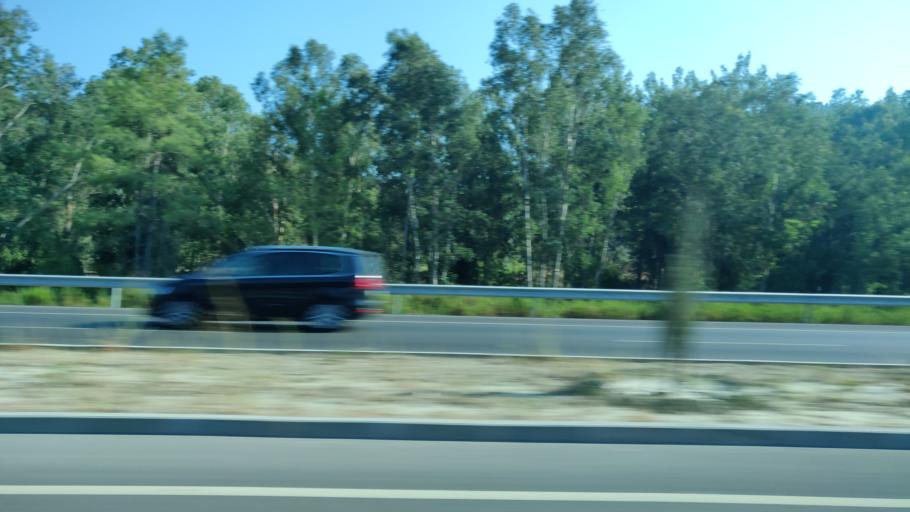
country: TR
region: Mugla
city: Goecek
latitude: 36.7606
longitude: 28.8784
